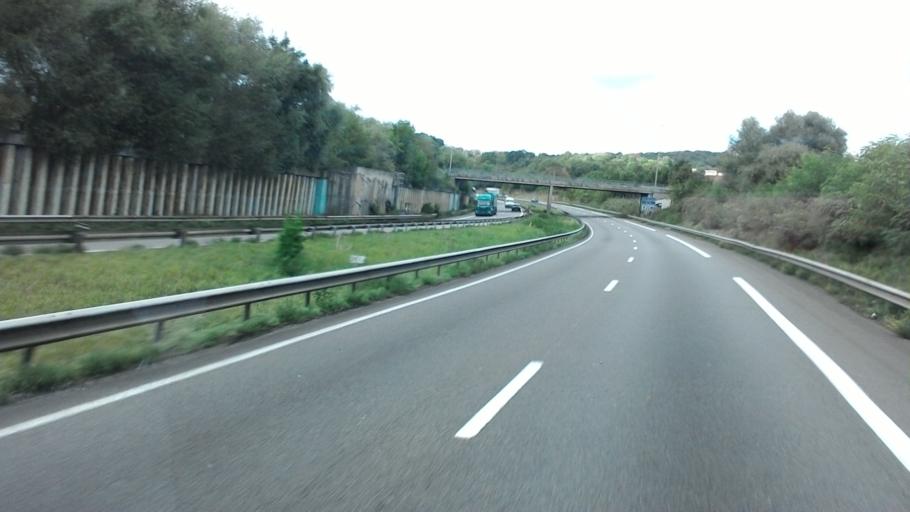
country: FR
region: Lorraine
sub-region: Departement de Meurthe-et-Moselle
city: Custines
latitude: 48.7880
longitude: 6.1424
